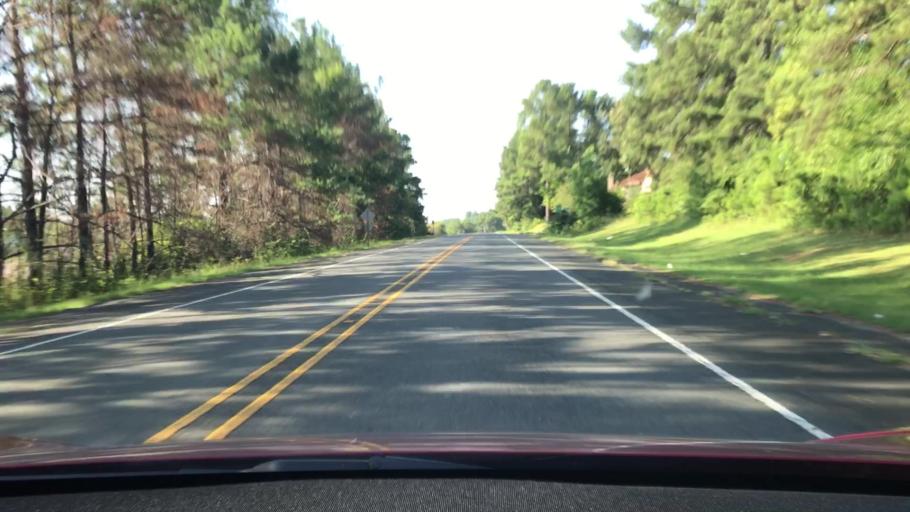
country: US
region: Louisiana
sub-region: Caddo Parish
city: Shreveport
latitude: 32.4509
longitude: -93.8439
